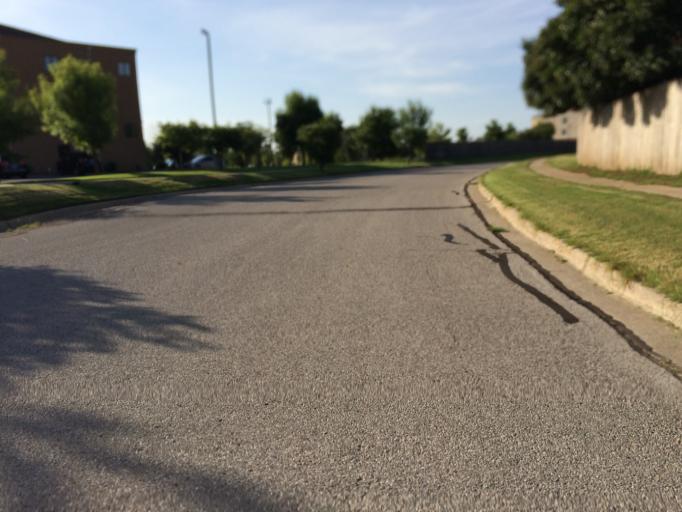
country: US
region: Oklahoma
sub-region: Cleveland County
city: Norman
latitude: 35.2280
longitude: -97.4885
